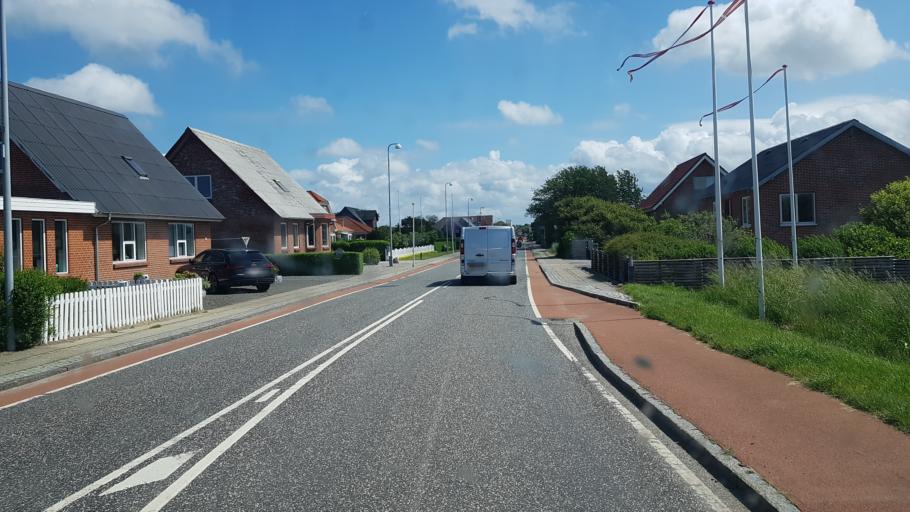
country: DK
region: Central Jutland
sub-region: Lemvig Kommune
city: Lemvig
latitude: 56.5547
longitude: 8.3896
